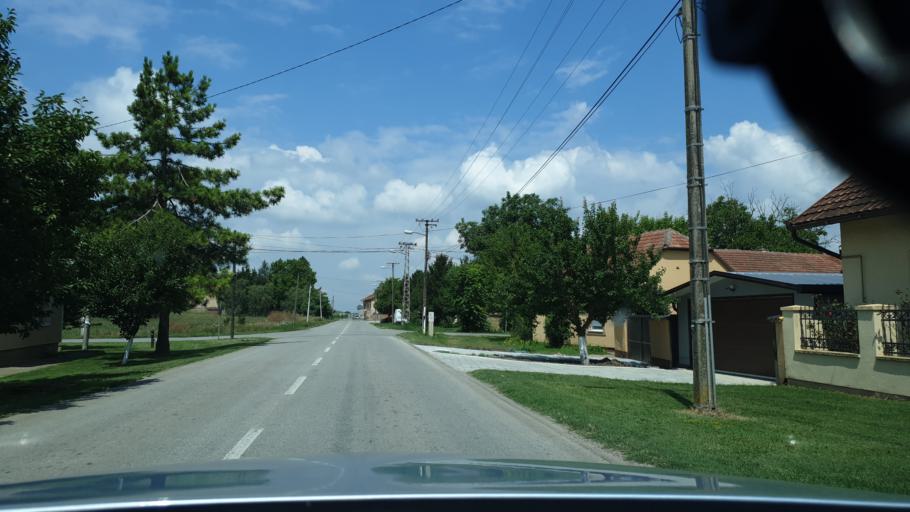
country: RS
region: Autonomna Pokrajina Vojvodina
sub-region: Juznobacki Okrug
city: Kovilj
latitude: 45.2399
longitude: 20.0263
